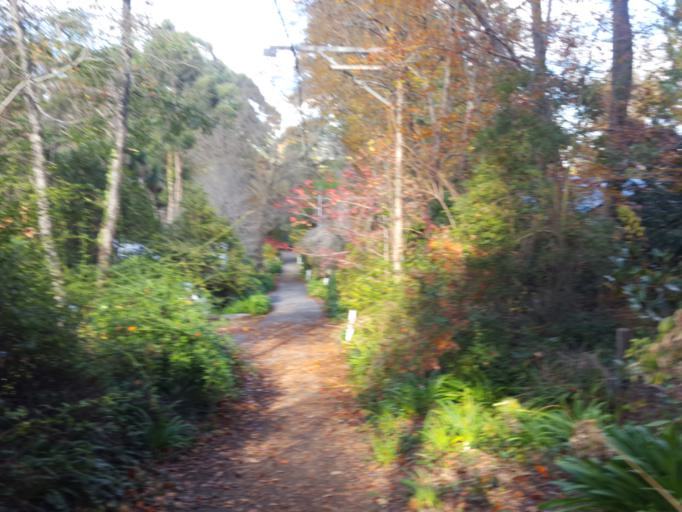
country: AU
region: South Australia
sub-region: Adelaide Hills
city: Crafers
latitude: -35.0021
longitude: 138.7050
